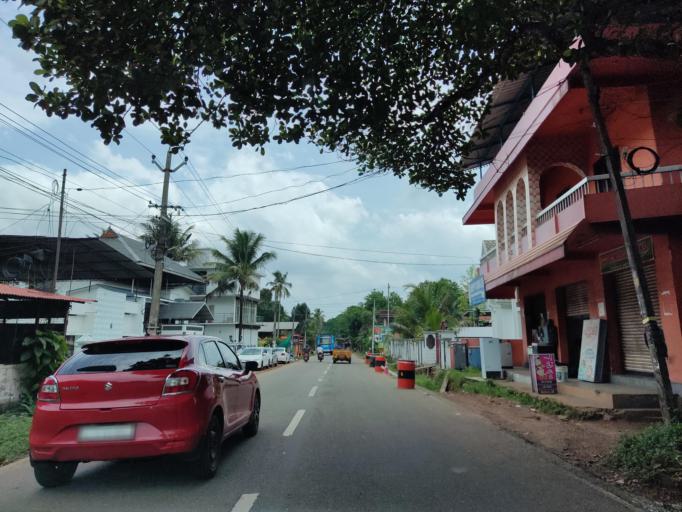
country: IN
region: Kerala
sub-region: Alappuzha
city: Mavelikara
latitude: 9.2279
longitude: 76.6252
